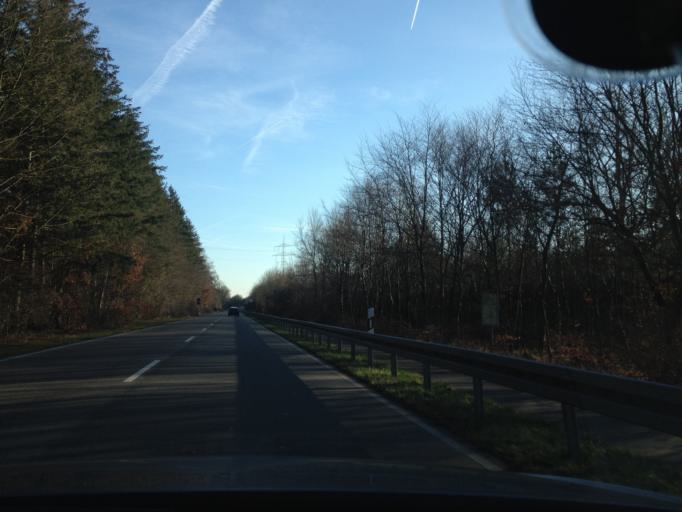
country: DE
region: Baden-Wuerttemberg
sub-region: Karlsruhe Region
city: Walldorf
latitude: 49.3267
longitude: 8.6226
